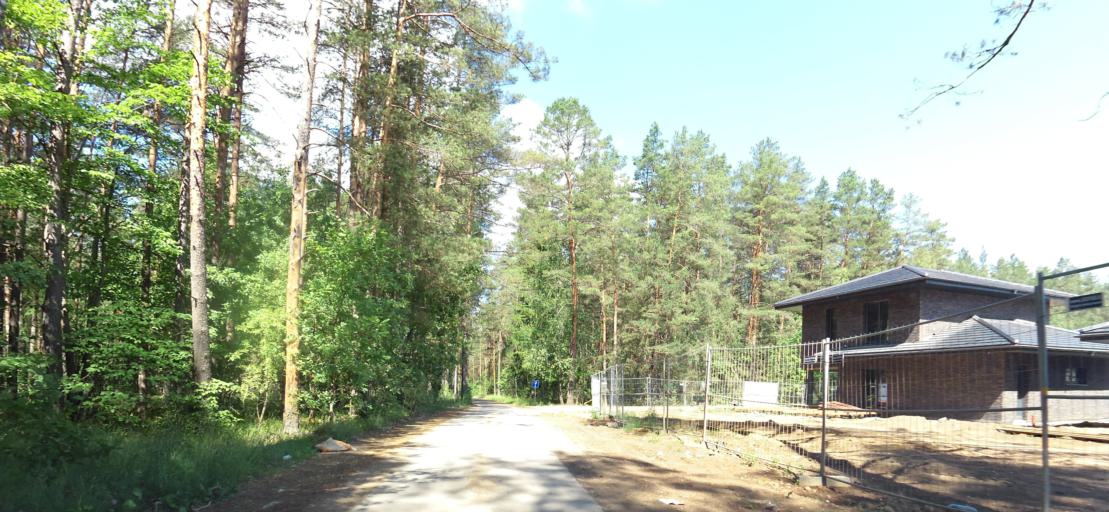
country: LT
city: Nemencine
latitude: 54.8139
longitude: 25.3882
